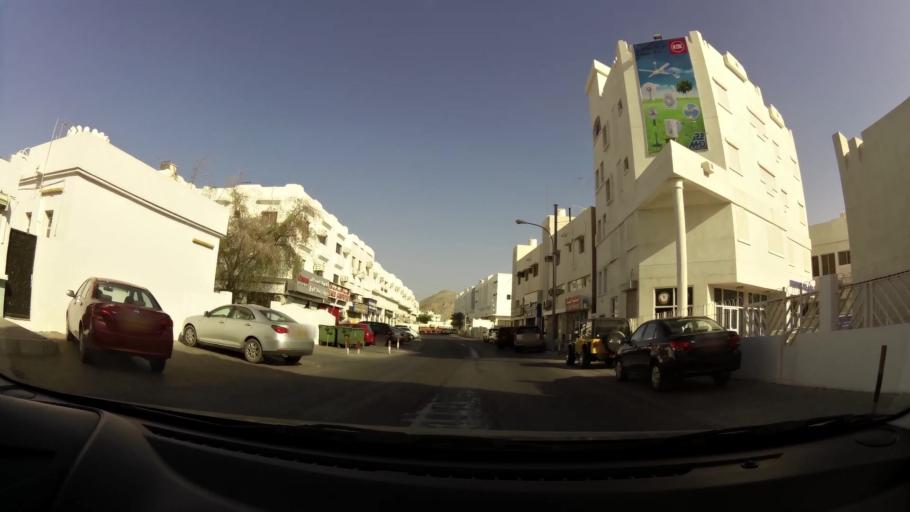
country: OM
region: Muhafazat Masqat
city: Muscat
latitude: 23.5933
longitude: 58.5479
